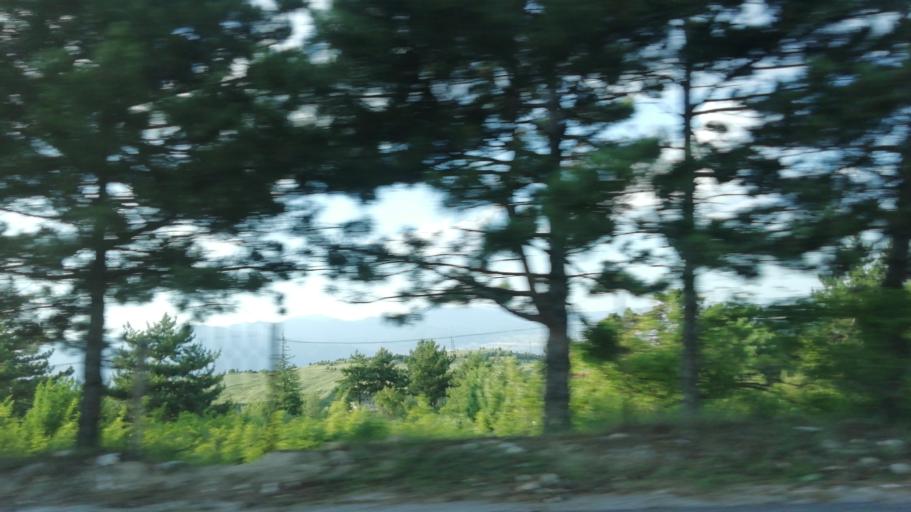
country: TR
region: Karabuk
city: Karabuk
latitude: 41.1285
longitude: 32.6093
